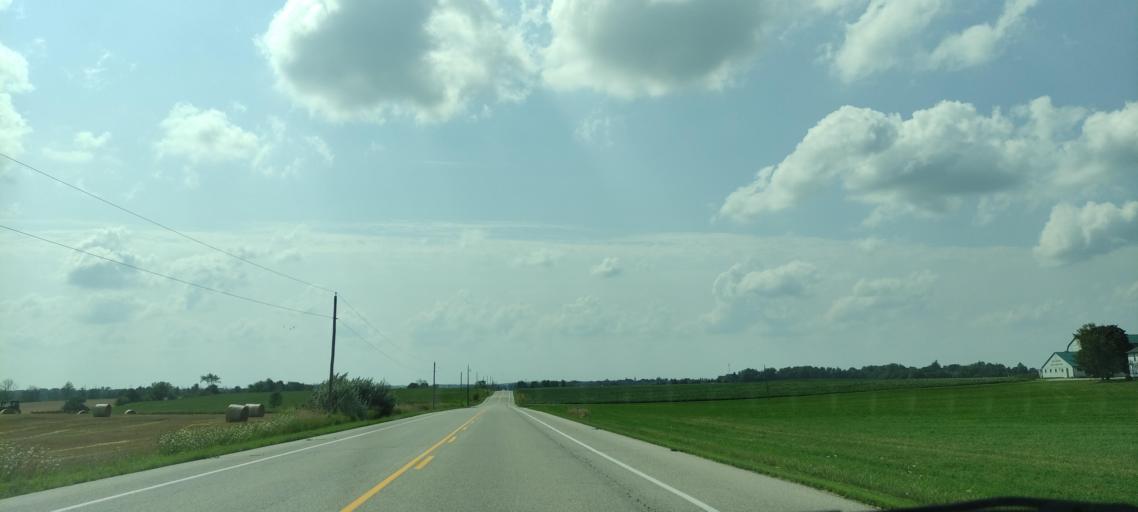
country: CA
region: Ontario
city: Waterloo
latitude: 43.4719
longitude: -80.7375
